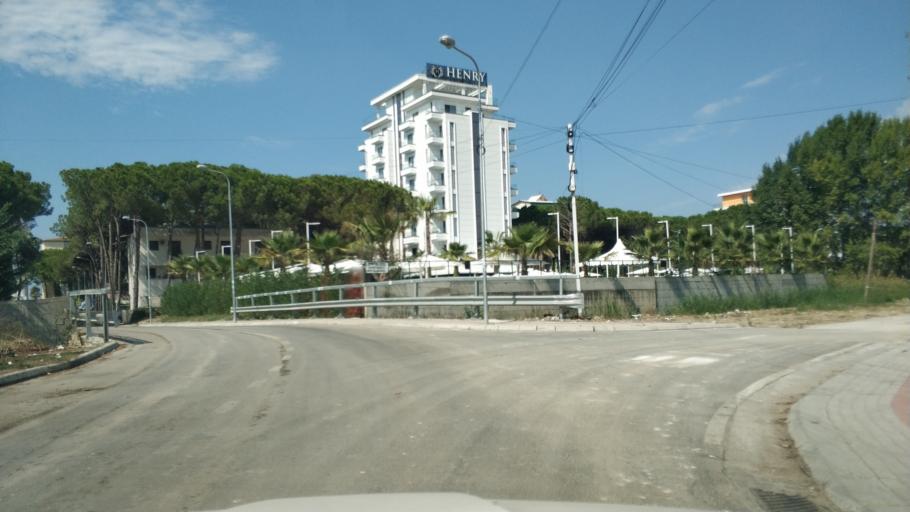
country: AL
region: Tirane
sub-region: Rrethi i Kavajes
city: Golem
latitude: 41.2382
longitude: 19.5194
